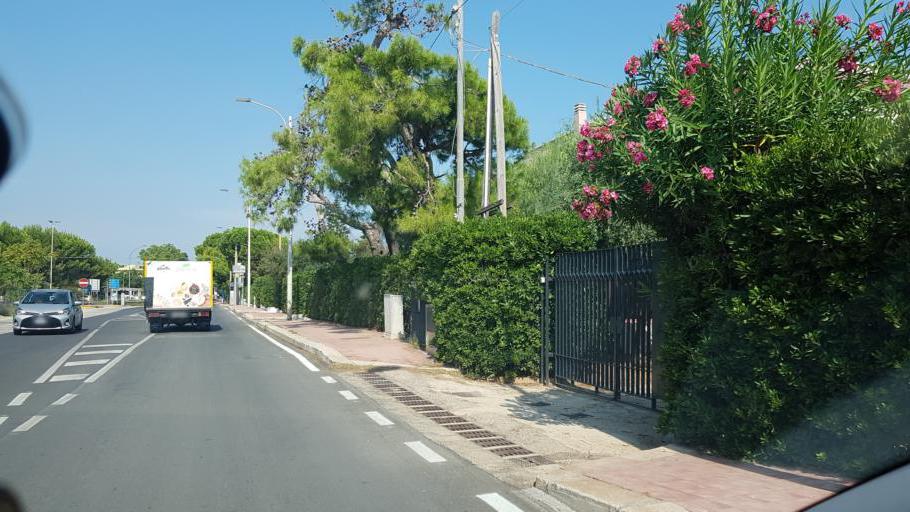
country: IT
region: Apulia
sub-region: Provincia di Brindisi
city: Fasano
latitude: 40.9043
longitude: 17.3517
